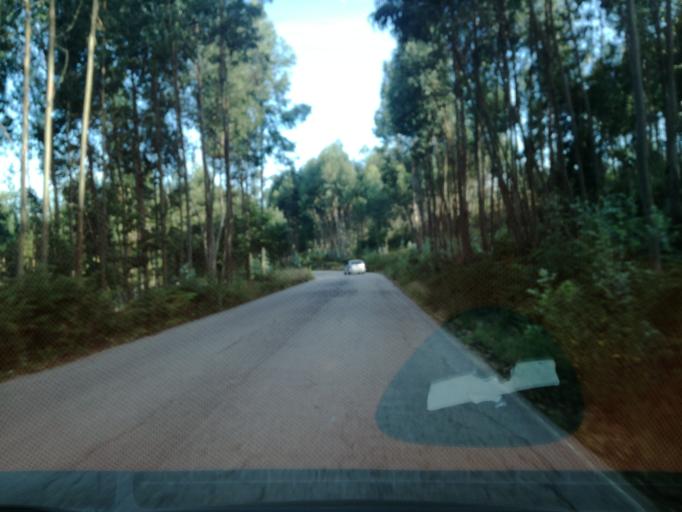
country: PT
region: Porto
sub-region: Valongo
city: Alfena
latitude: 41.2640
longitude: -8.5252
